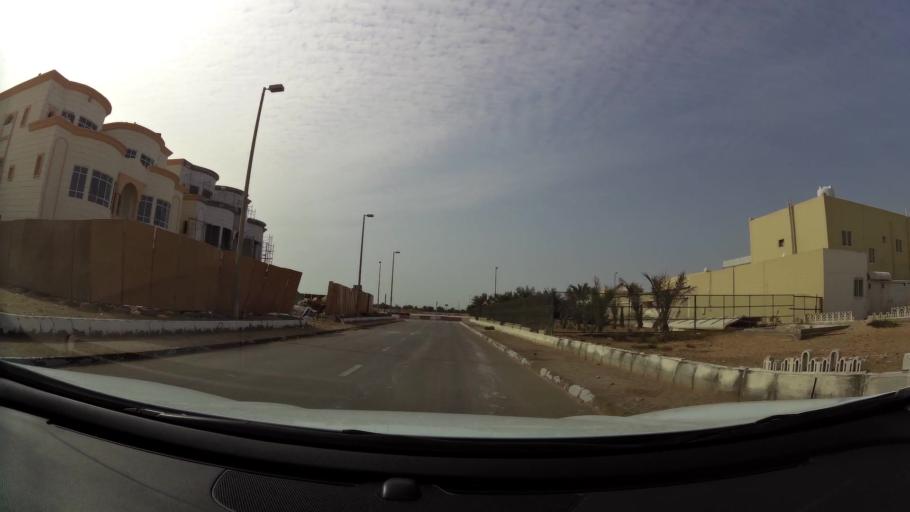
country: AE
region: Abu Dhabi
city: Abu Dhabi
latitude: 24.5947
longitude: 54.6950
